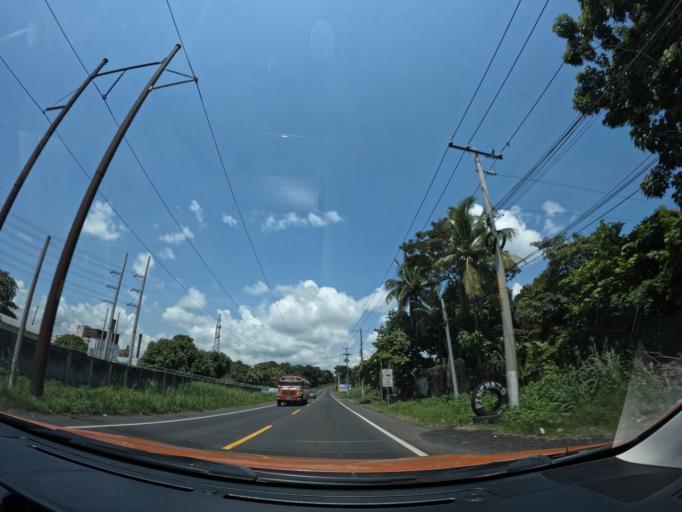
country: GT
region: Escuintla
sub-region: Municipio de Escuintla
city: Escuintla
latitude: 14.2632
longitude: -90.7967
